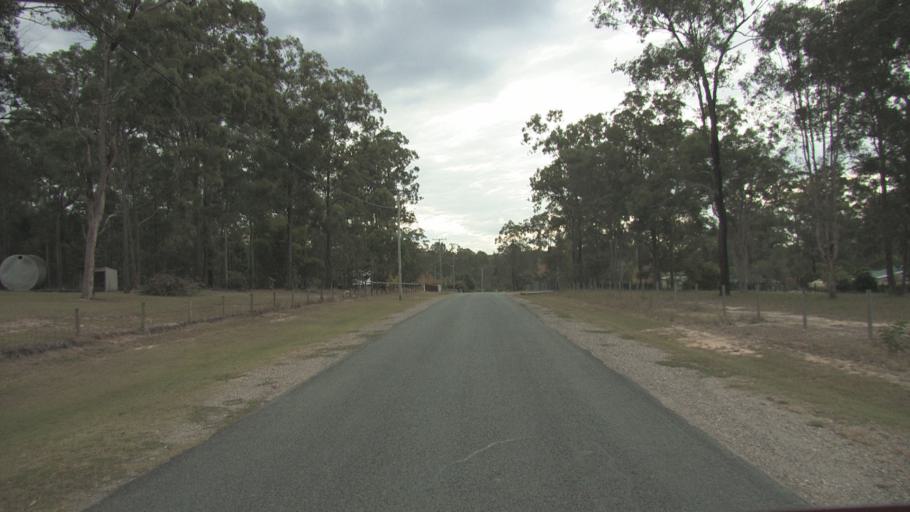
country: AU
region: Queensland
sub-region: Logan
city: Chambers Flat
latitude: -27.7928
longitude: 153.1170
